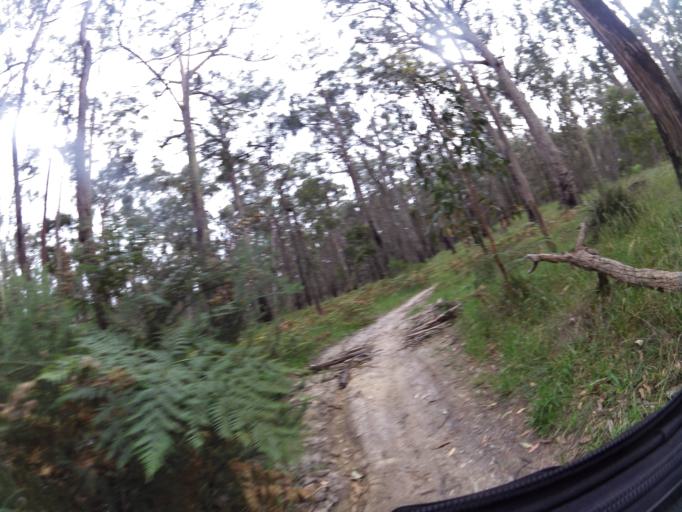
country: AU
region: Victoria
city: Brown Hill
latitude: -37.5254
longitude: 143.9055
